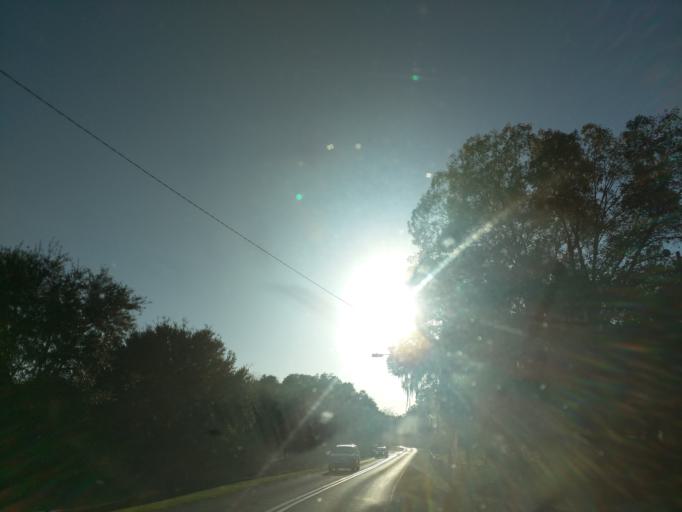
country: US
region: Florida
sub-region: Leon County
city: Tallahassee
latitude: 30.4438
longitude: -84.2168
